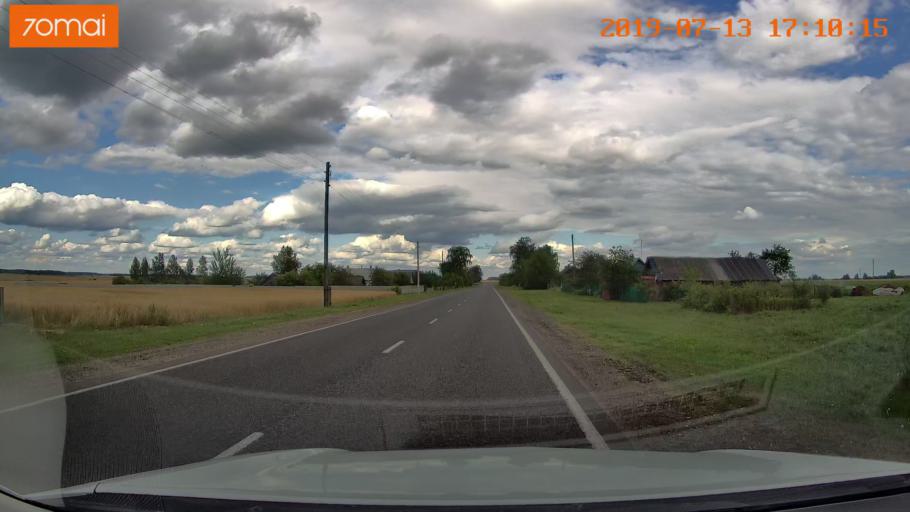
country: BY
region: Mogilev
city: Babruysk
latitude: 53.2688
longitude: 29.2777
